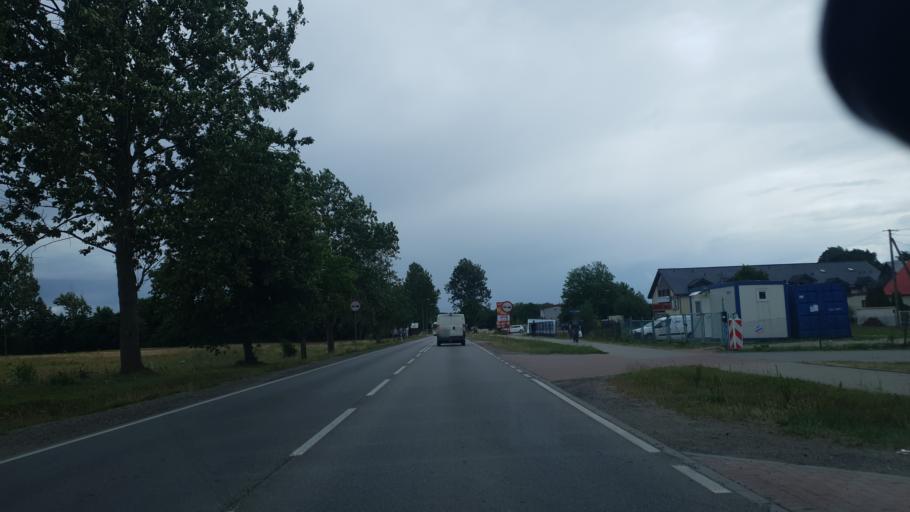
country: PL
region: Pomeranian Voivodeship
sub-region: Powiat kartuski
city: Banino
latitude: 54.4193
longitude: 18.3788
